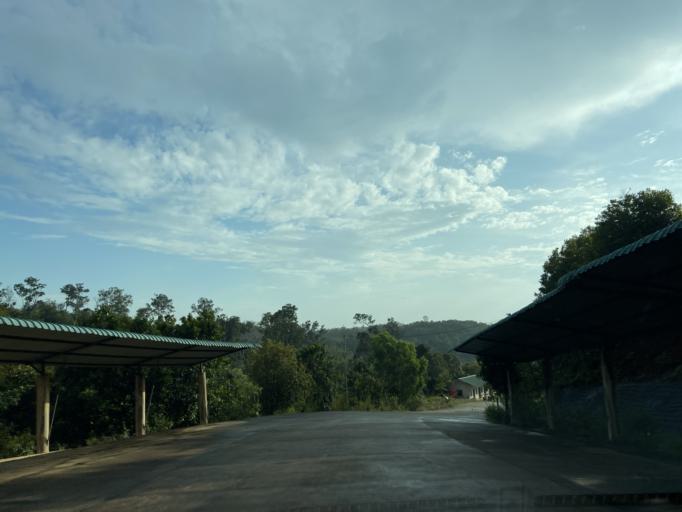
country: ID
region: Riau Islands
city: Tanjungpinang
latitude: 0.8939
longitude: 104.1230
